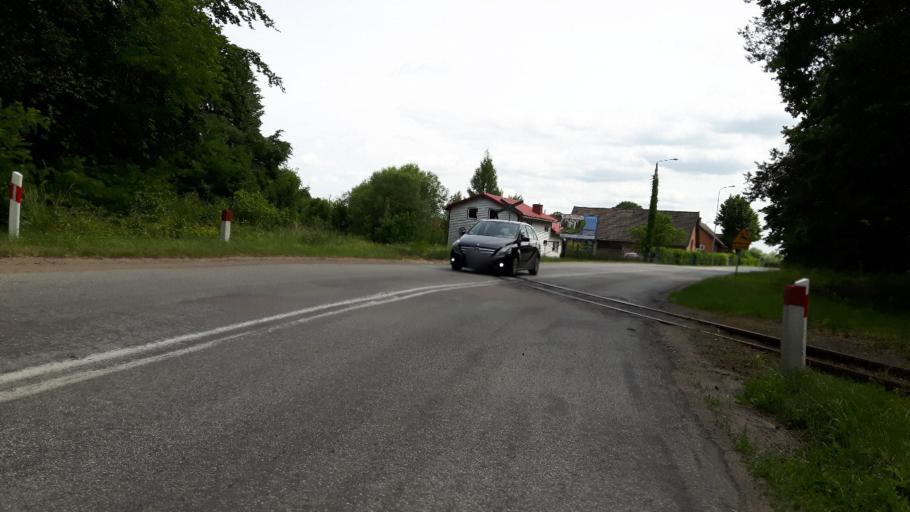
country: PL
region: Pomeranian Voivodeship
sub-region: Powiat nowodworski
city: Stegna
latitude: 54.3345
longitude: 19.0132
